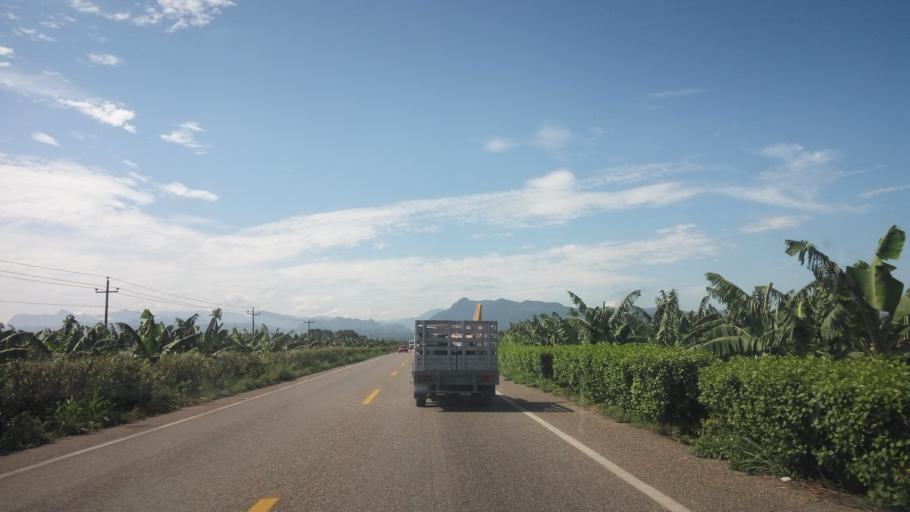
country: MX
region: Tabasco
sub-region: Teapa
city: Eureka y Belen
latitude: 17.6121
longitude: -92.9650
